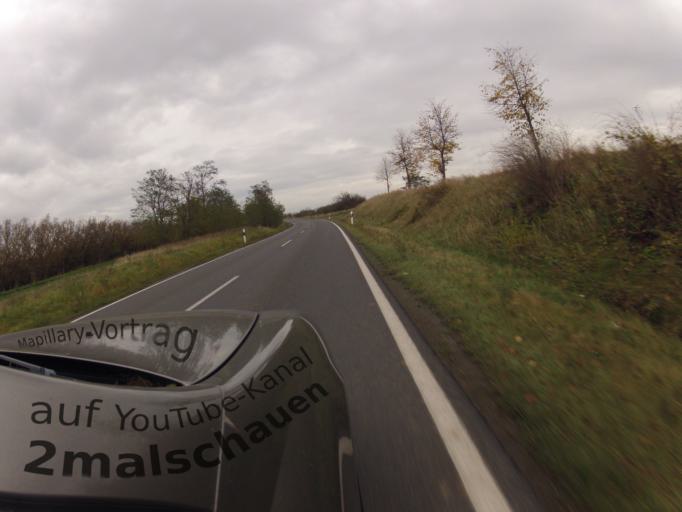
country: DE
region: Saxony-Anhalt
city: Beesenlaublingen
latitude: 51.7146
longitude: 11.7063
